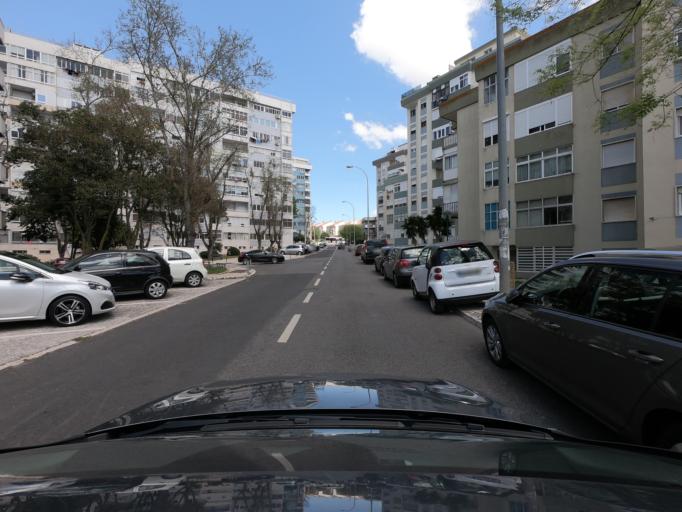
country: PT
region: Lisbon
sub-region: Oeiras
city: Oeiras
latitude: 38.6944
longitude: -9.3077
